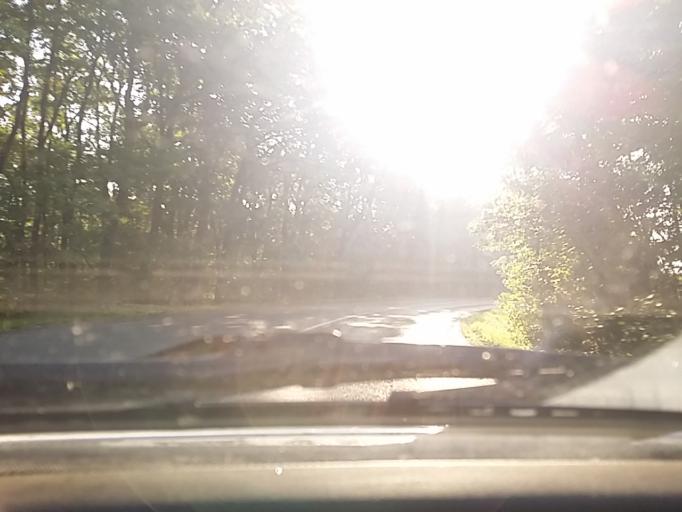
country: HU
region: Pest
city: Nagykovacsi
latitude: 47.7189
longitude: 19.0081
